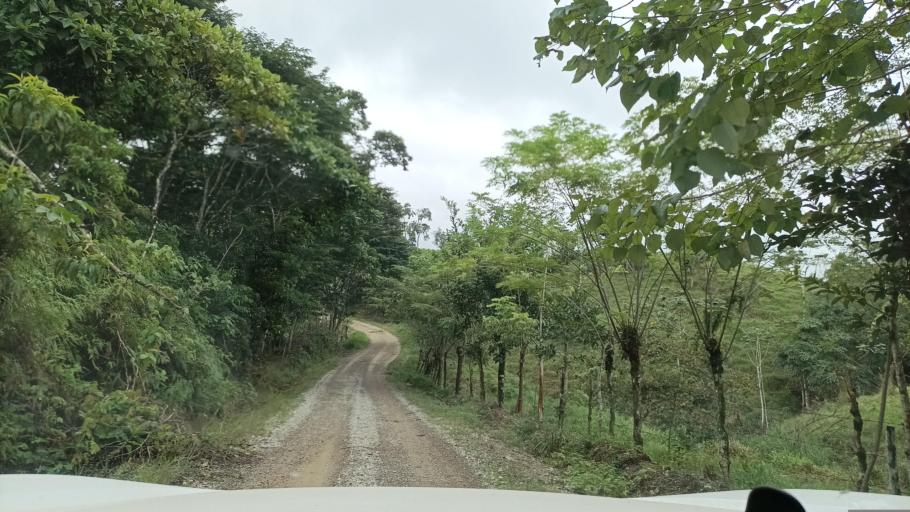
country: MX
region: Veracruz
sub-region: Uxpanapa
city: Poblado 10
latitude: 17.4324
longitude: -94.4173
